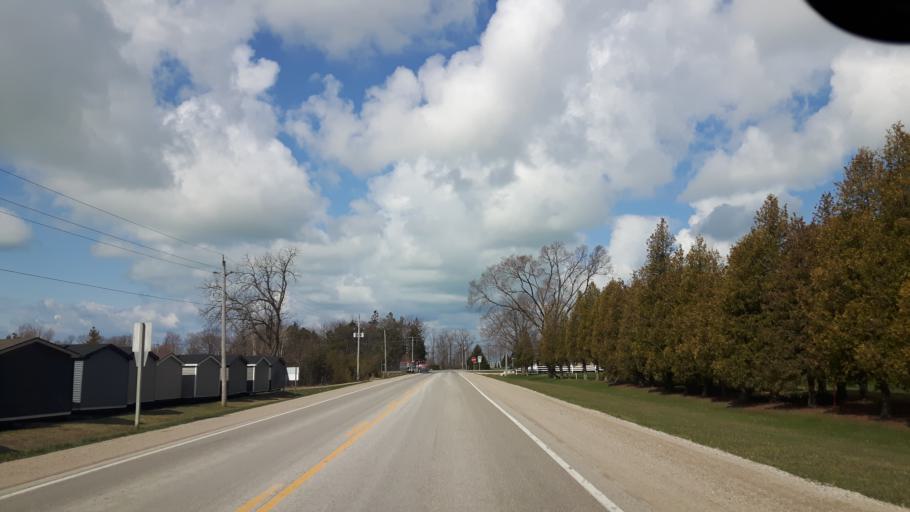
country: CA
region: Ontario
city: Bluewater
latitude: 43.5870
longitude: -81.7031
